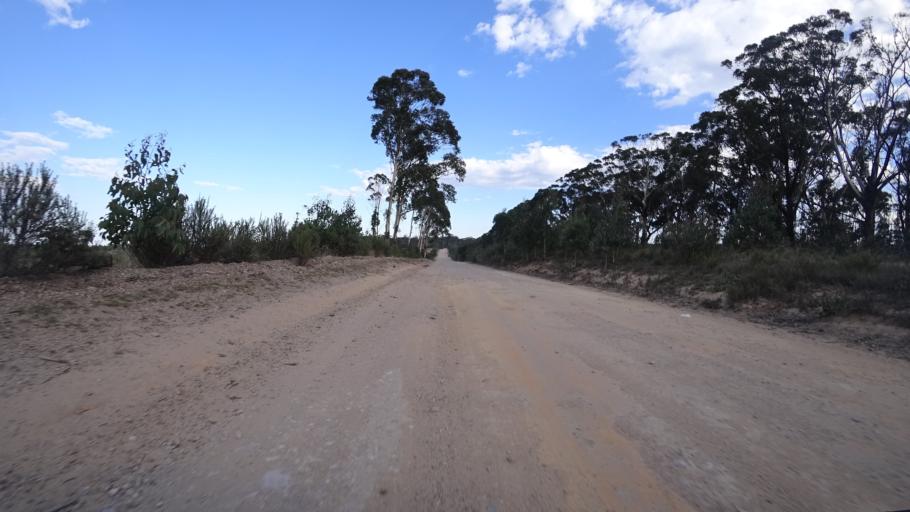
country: AU
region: New South Wales
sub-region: Lithgow
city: Lithgow
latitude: -33.4125
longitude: 150.2012
